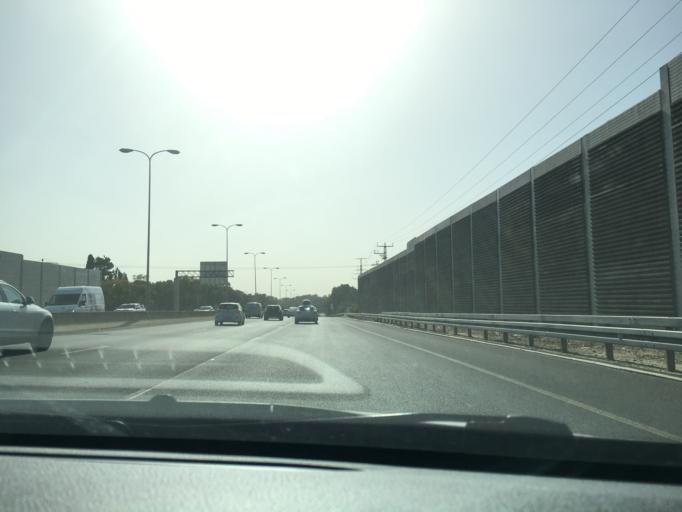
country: IL
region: Central District
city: Hod HaSharon
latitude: 32.1635
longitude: 34.8786
